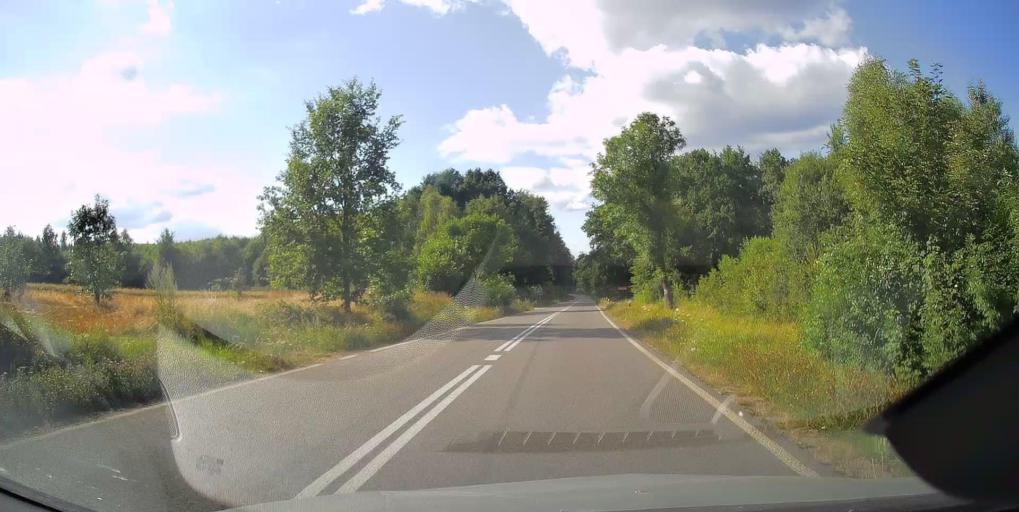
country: PL
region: Swietokrzyskie
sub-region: Powiat skarzyski
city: Suchedniow
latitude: 50.9900
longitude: 20.8630
